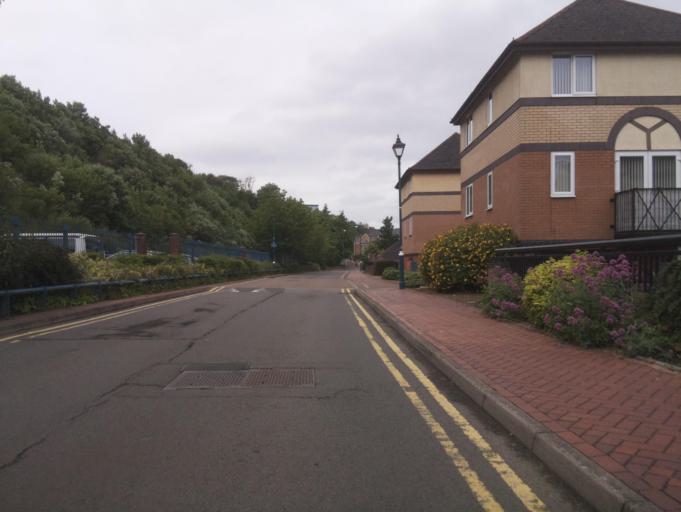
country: GB
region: Wales
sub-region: Vale of Glamorgan
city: Penarth
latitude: 51.4442
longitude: -3.1757
